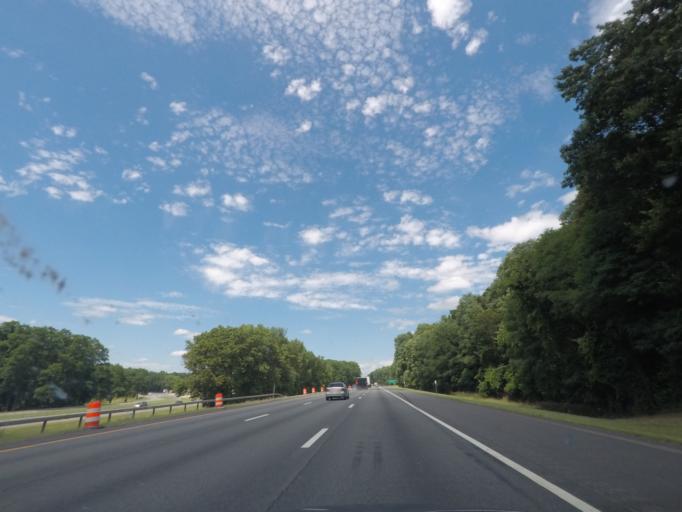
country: US
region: New York
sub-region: Albany County
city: Westmere
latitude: 42.7422
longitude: -73.9135
